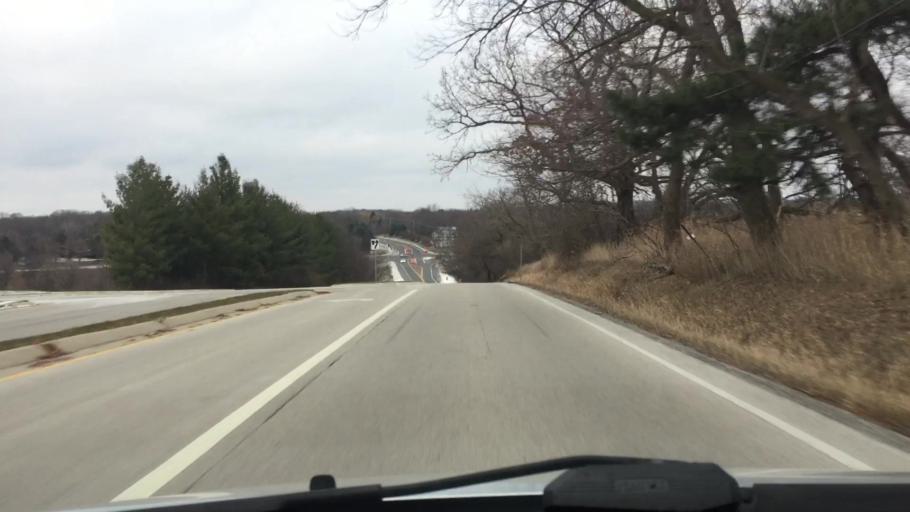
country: US
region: Wisconsin
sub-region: Waukesha County
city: Pewaukee
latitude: 43.1023
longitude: -88.2695
